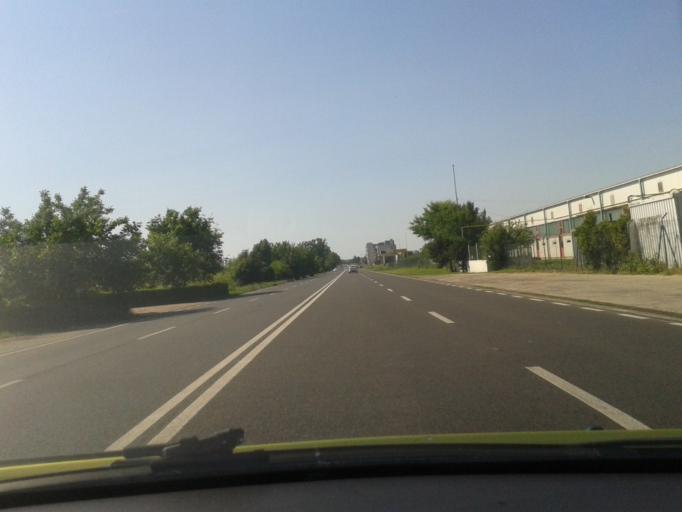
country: RO
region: Constanta
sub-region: Municipiul Mangalia
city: Mangalia
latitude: 43.8357
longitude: 28.5771
